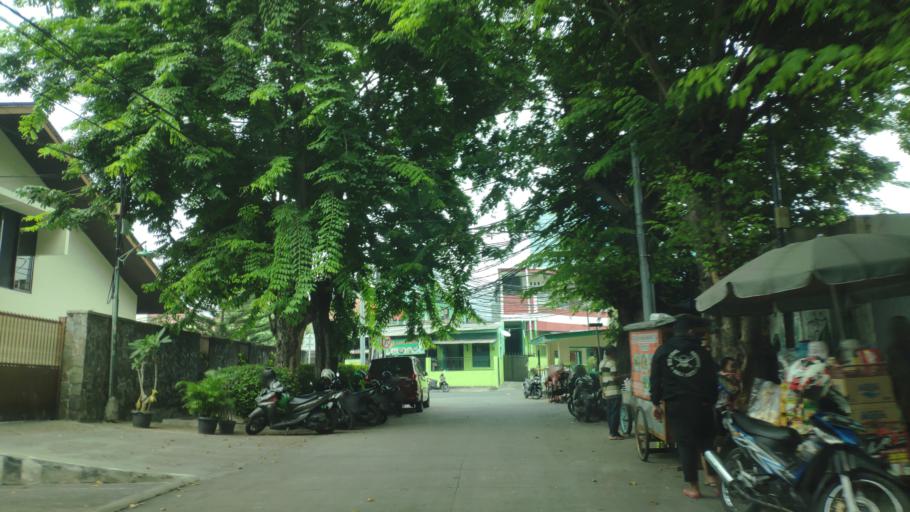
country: ID
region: Jakarta Raya
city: Jakarta
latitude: -6.1902
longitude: 106.8022
